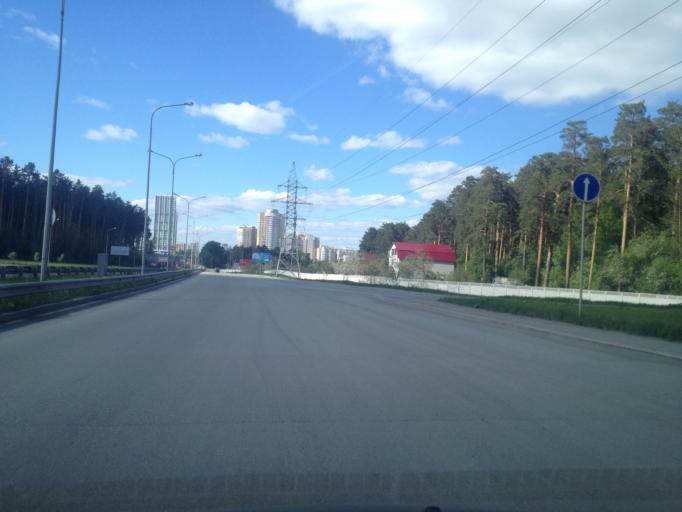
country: RU
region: Sverdlovsk
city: Sovkhoznyy
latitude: 56.7918
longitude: 60.5976
